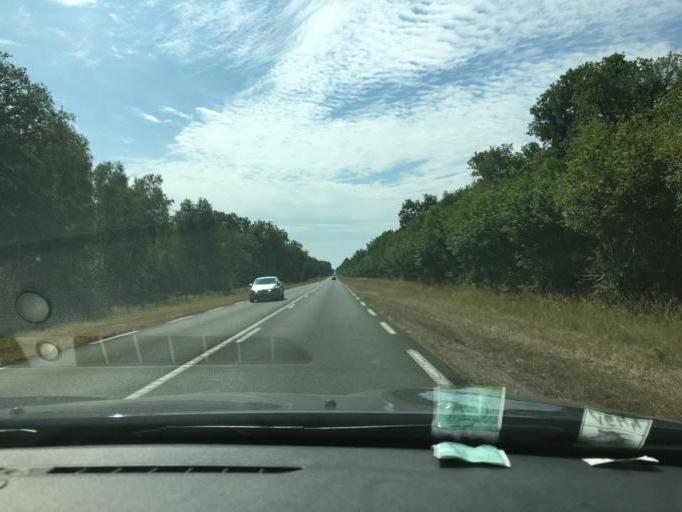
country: FR
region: Centre
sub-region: Departement du Loiret
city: La Ferte-Saint-Aubin
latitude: 47.6850
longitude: 1.9613
